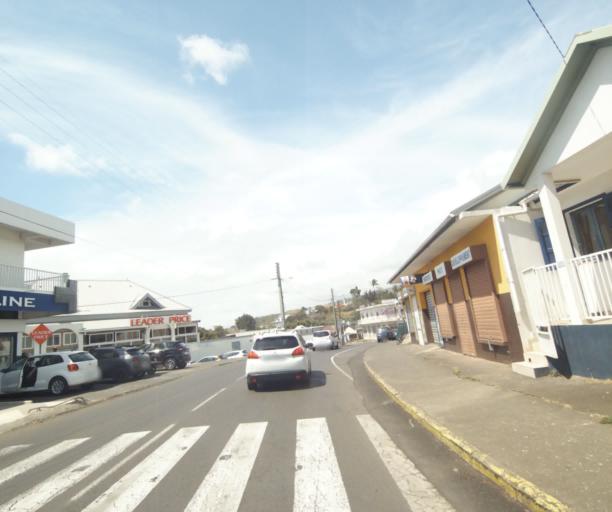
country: RE
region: Reunion
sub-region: Reunion
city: Trois-Bassins
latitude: -21.0818
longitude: 55.2700
